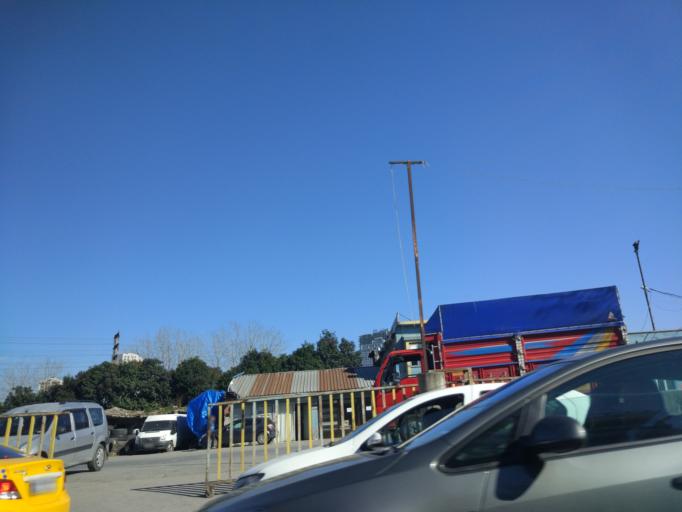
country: TR
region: Istanbul
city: Mahmutbey
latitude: 41.0264
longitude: 28.8074
